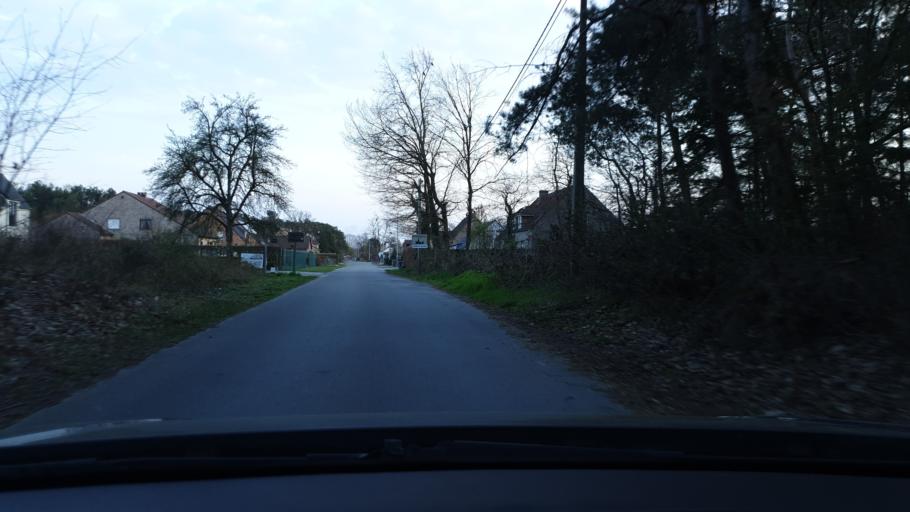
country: BE
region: Flanders
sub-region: Provincie Antwerpen
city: Geel
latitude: 51.1314
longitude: 5.0009
